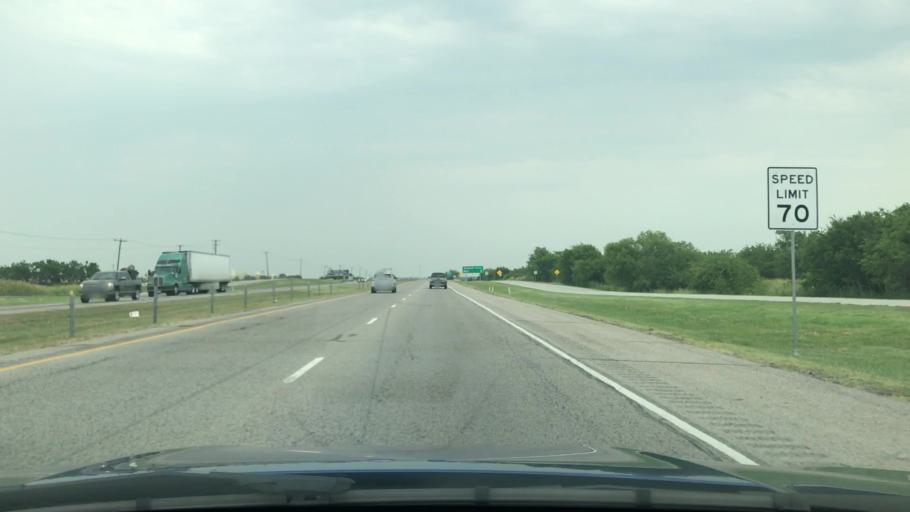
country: US
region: Texas
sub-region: Kaufman County
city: Talty
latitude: 32.7401
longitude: -96.4036
